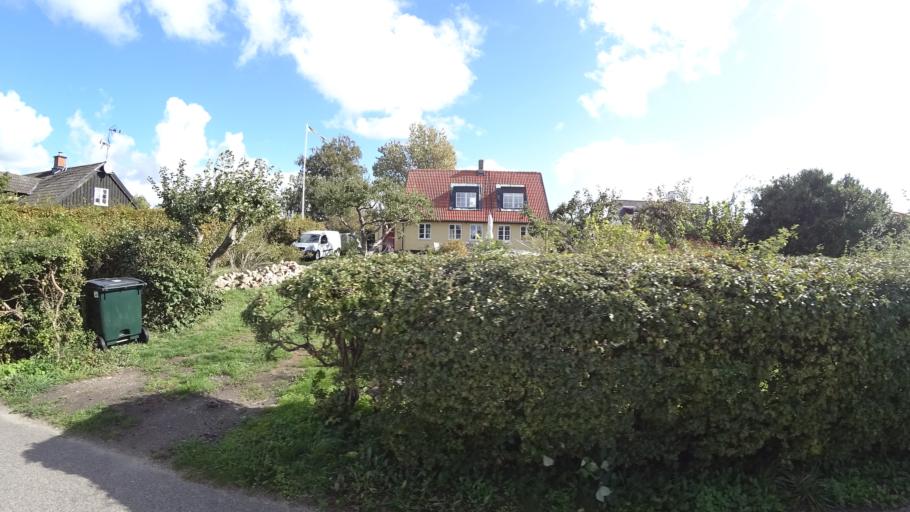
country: SE
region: Skane
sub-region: Kavlinge Kommun
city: Hofterup
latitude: 55.7532
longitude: 12.9053
